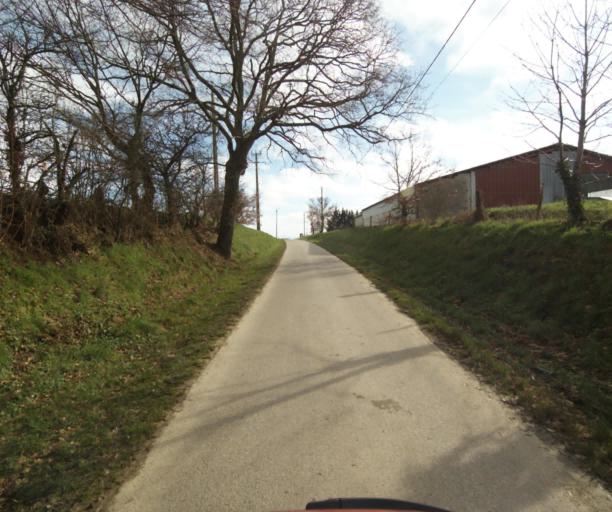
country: FR
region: Midi-Pyrenees
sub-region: Departement de l'Ariege
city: La Tour-du-Crieu
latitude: 43.1386
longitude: 1.6973
